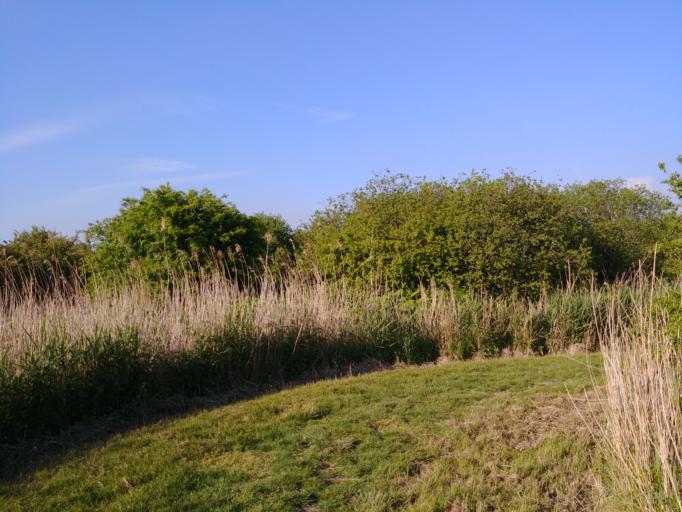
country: NL
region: South Holland
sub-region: Gemeente Rotterdam
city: Hoek van Holland
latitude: 51.9206
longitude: 4.0810
